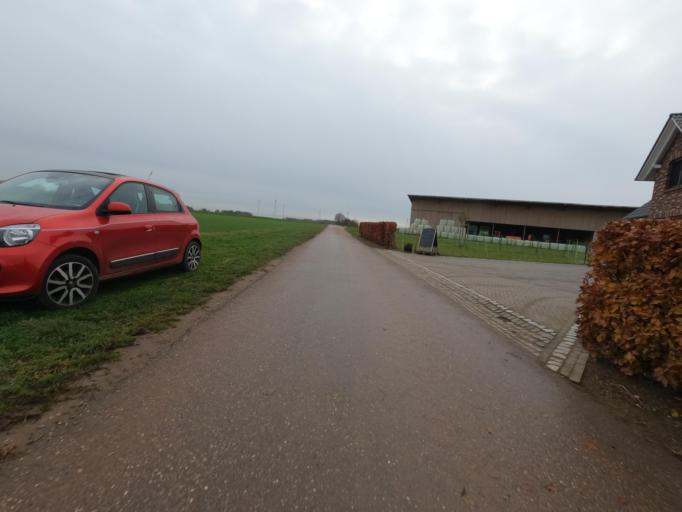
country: DE
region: North Rhine-Westphalia
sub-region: Regierungsbezirk Koln
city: Heinsberg
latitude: 51.0397
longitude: 6.1357
